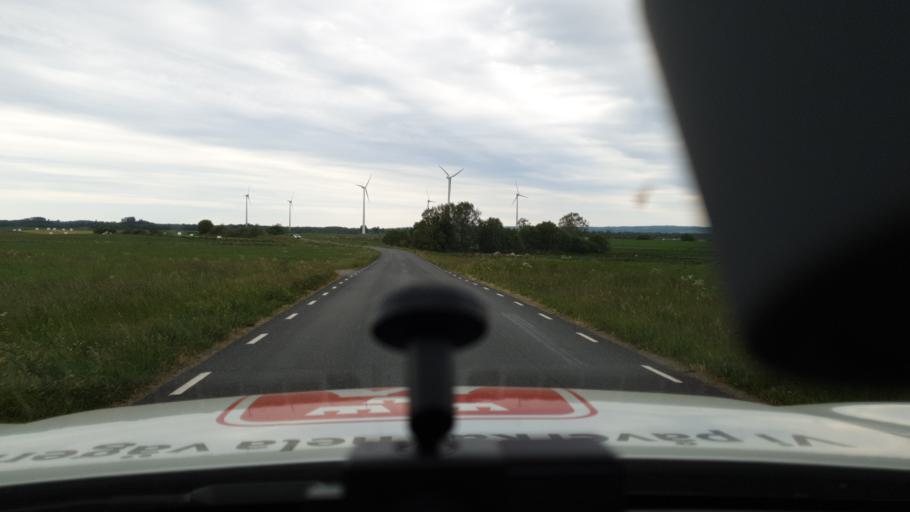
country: SE
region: Vaestra Goetaland
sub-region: Falkopings Kommun
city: Falkoeping
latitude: 58.0901
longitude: 13.5141
